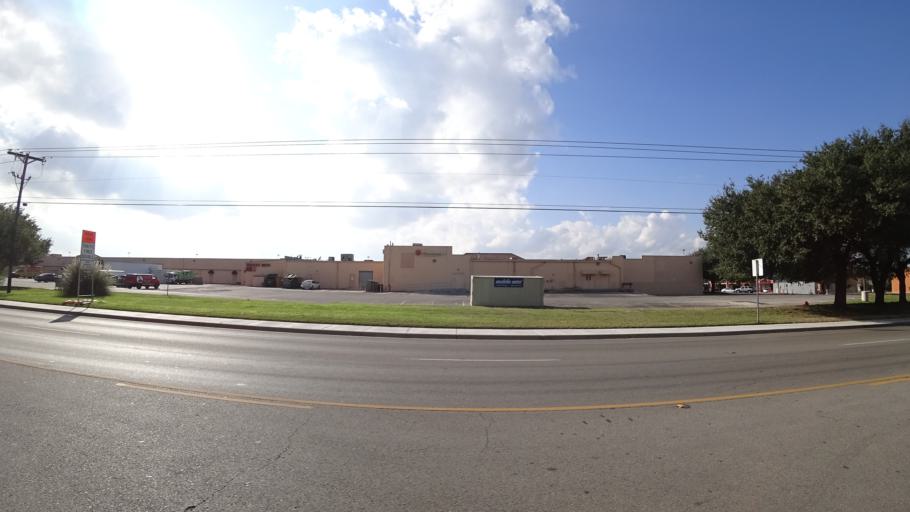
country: US
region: Texas
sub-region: Williamson County
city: Round Rock
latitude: 30.4956
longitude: -97.6758
